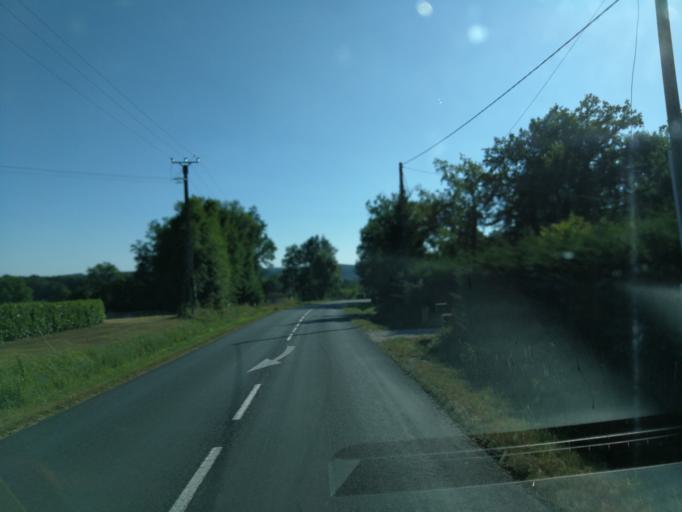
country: FR
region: Midi-Pyrenees
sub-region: Departement du Lot
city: Gourdon
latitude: 44.7189
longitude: 1.3651
